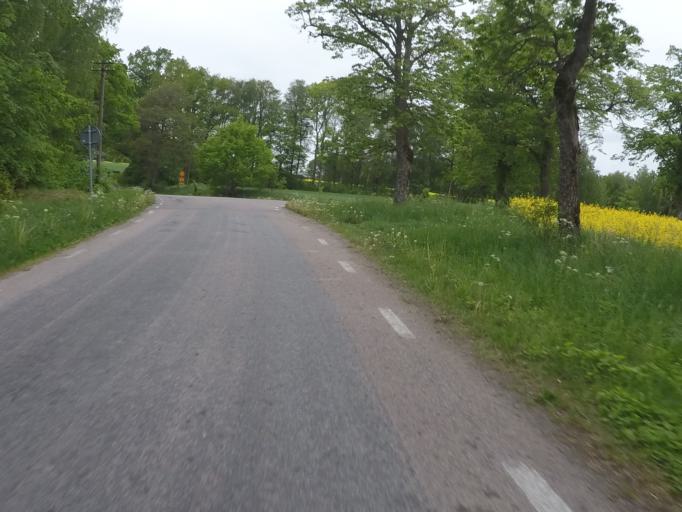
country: SE
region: Vaestmanland
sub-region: Hallstahammars Kommun
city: Kolback
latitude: 59.5526
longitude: 16.2651
